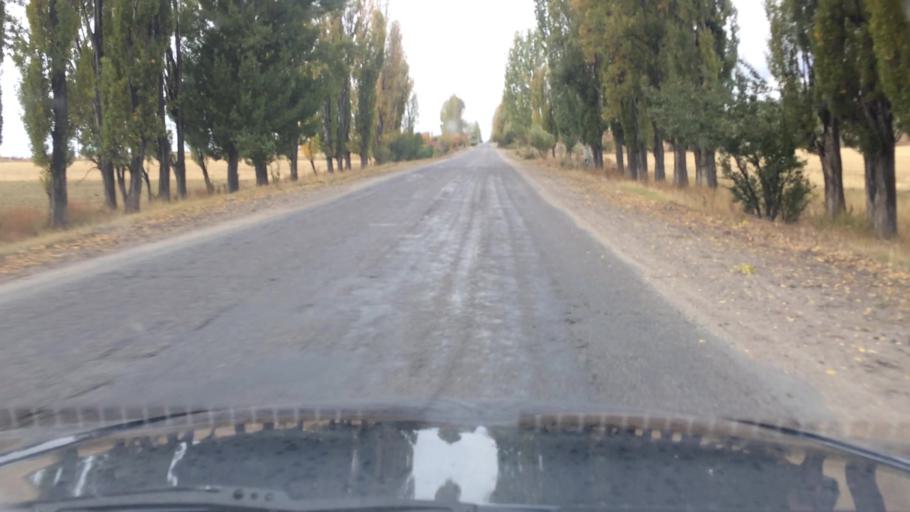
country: KG
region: Ysyk-Koel
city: Pokrovka
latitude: 42.7364
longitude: 77.9571
